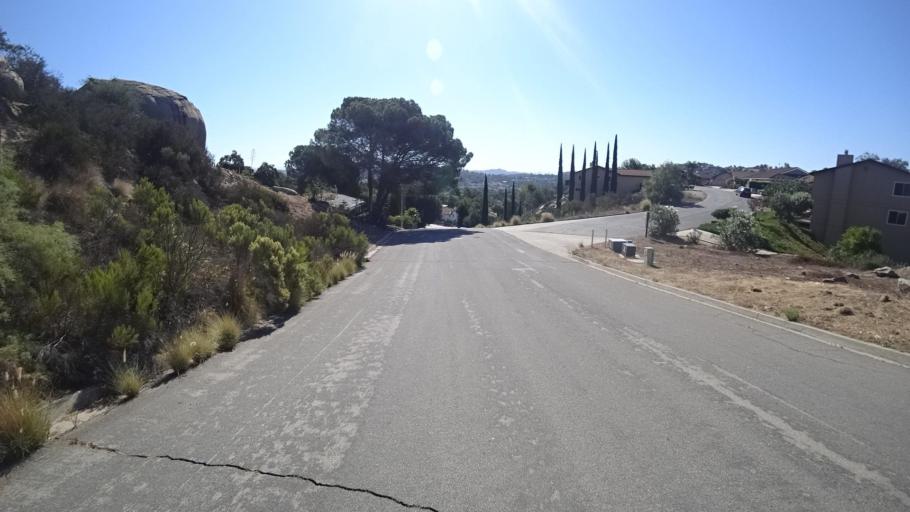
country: US
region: California
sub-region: San Diego County
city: Hidden Meadows
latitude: 33.2189
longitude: -117.1198
